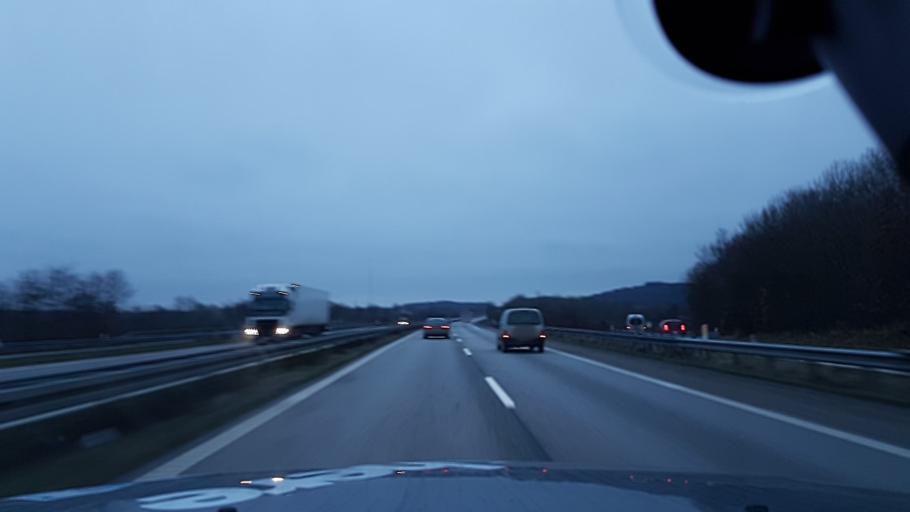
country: DK
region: Zealand
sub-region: Vordingborg Kommune
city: Orslev
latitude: 55.0780
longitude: 11.9568
